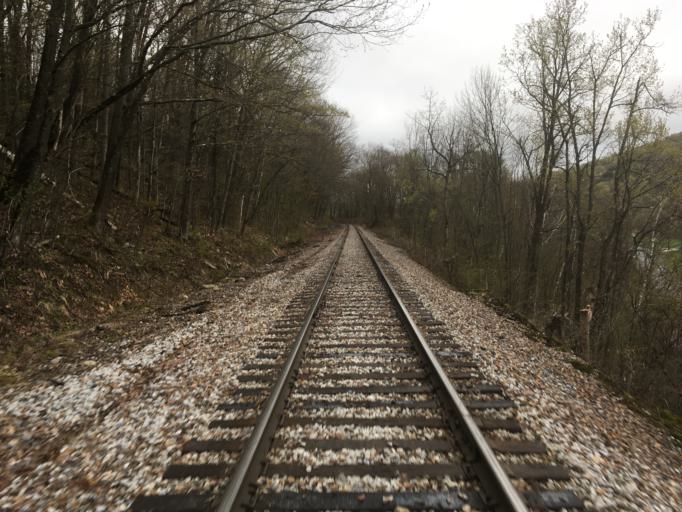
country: US
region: Vermont
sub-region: Rutland County
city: Rutland
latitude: 43.4826
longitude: -72.8766
